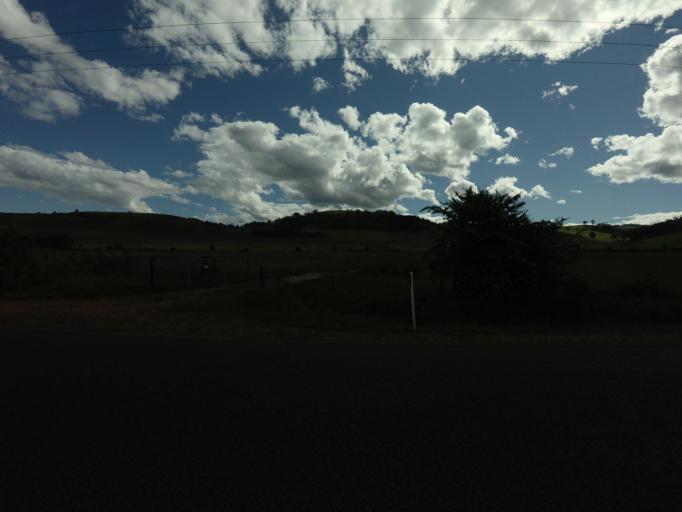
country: AU
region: Tasmania
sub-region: Brighton
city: Bridgewater
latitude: -42.5282
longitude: 147.3599
